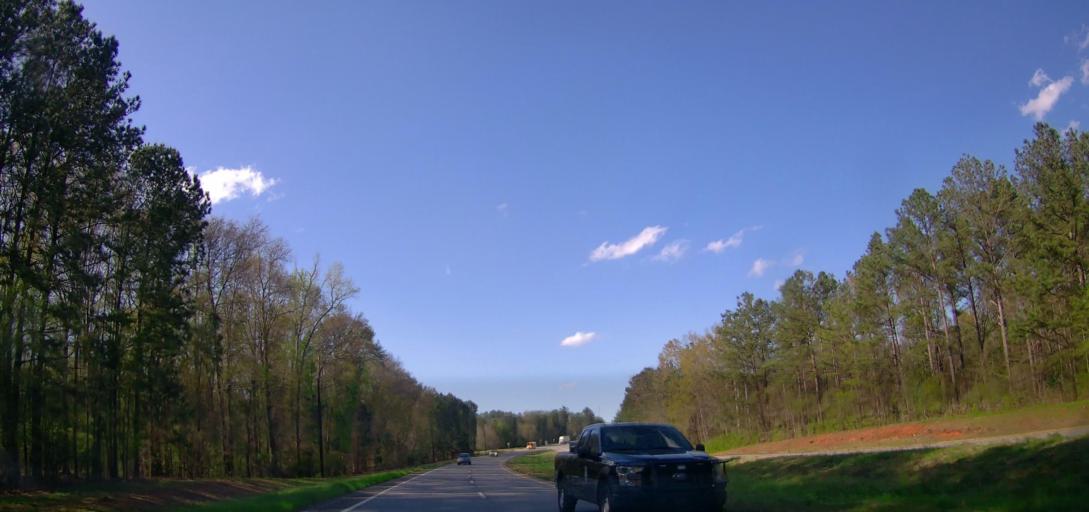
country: US
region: Georgia
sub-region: Baldwin County
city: Hardwick
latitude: 33.0419
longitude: -83.2552
